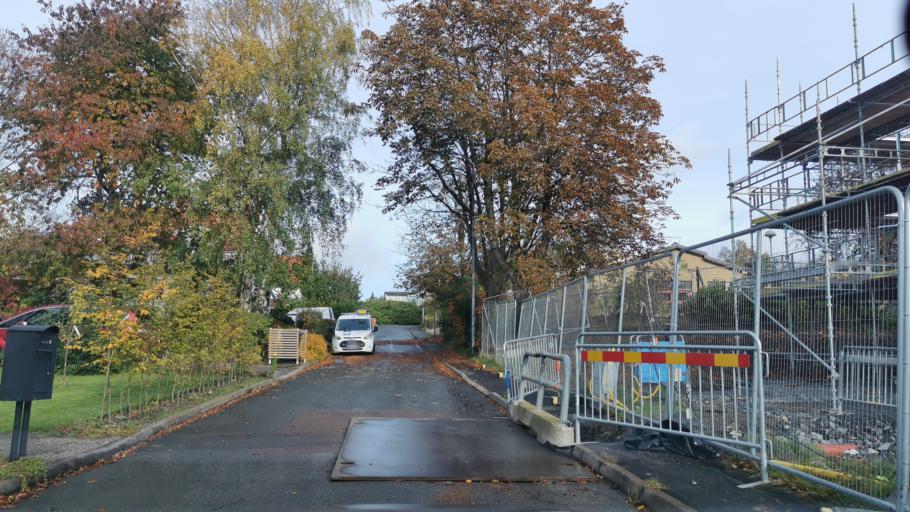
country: SE
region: Vaestra Goetaland
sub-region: Partille Kommun
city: Partille
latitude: 57.7294
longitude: 12.0852
